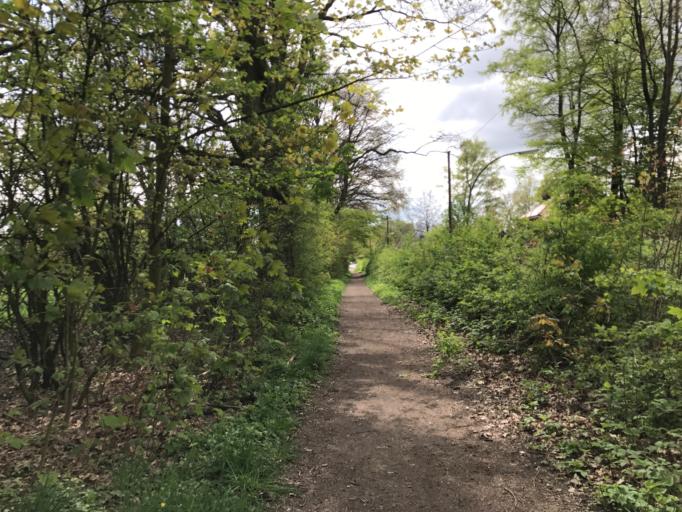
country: DE
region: Schleswig-Holstein
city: Stapelfeld
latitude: 53.6383
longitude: 10.1790
